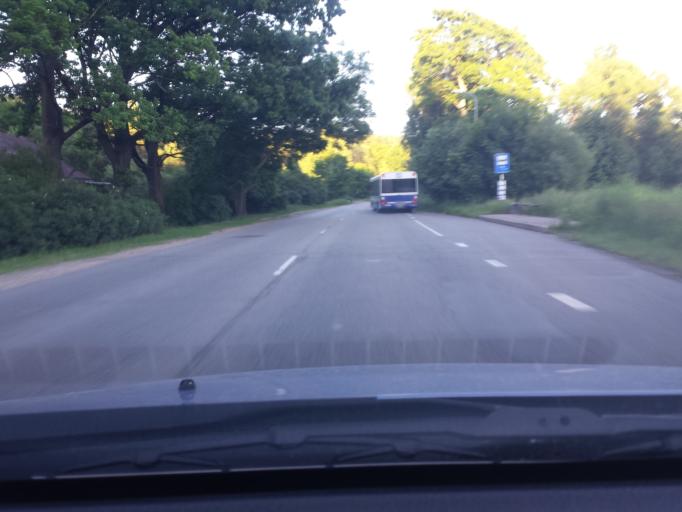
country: LV
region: Riga
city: Jaunciems
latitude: 57.0527
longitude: 24.1678
